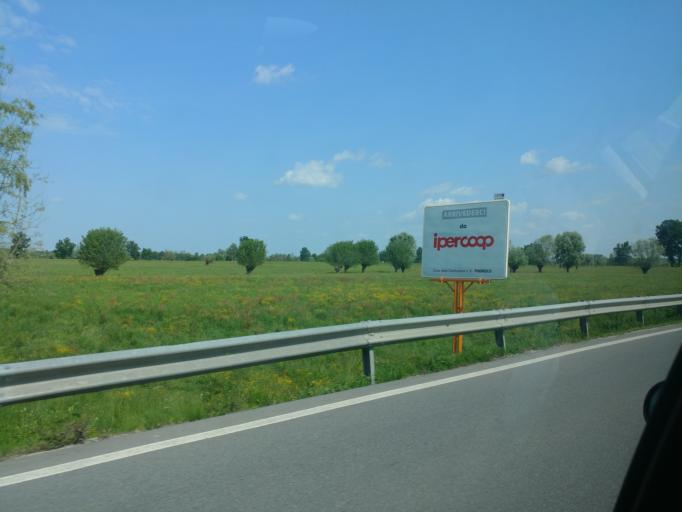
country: IT
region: Piedmont
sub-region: Provincia di Cuneo
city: Carde
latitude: 44.7253
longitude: 7.4343
